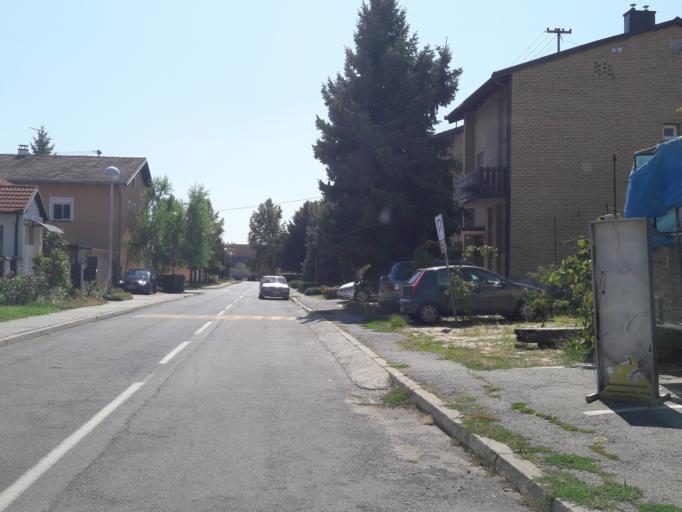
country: HR
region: Osjecko-Baranjska
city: Visnjevac
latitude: 45.5647
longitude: 18.6387
